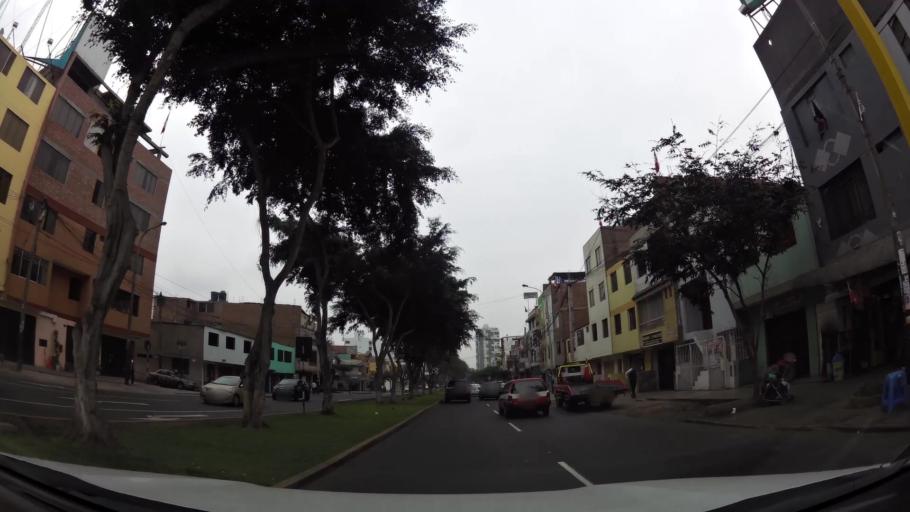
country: PE
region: Lima
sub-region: Lima
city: Surco
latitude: -12.1124
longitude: -77.0073
